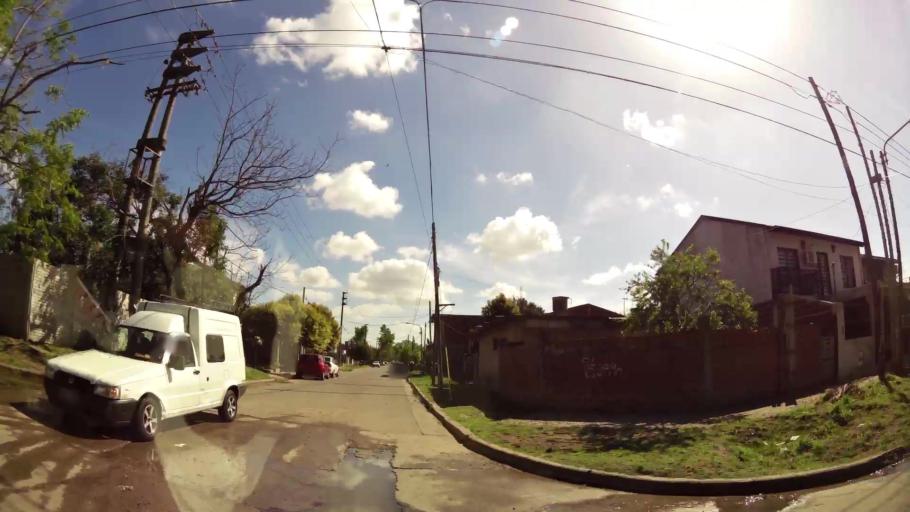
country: AR
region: Buenos Aires
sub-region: Partido de Quilmes
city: Quilmes
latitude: -34.7988
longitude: -58.2534
